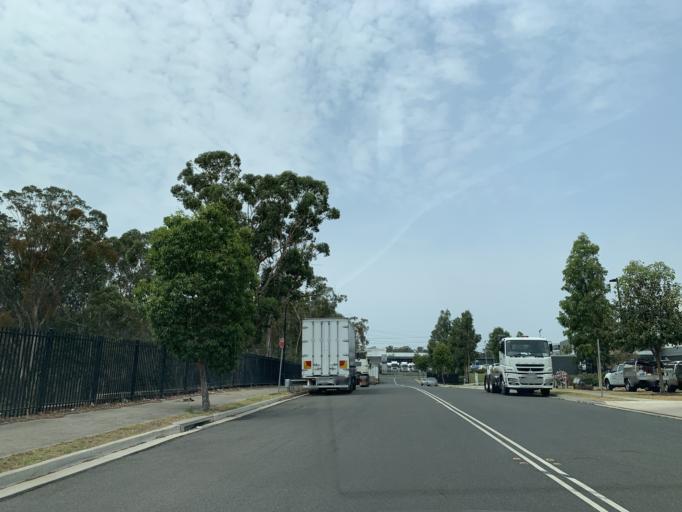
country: AU
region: New South Wales
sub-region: Blacktown
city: Blacktown
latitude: -33.7998
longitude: 150.9000
